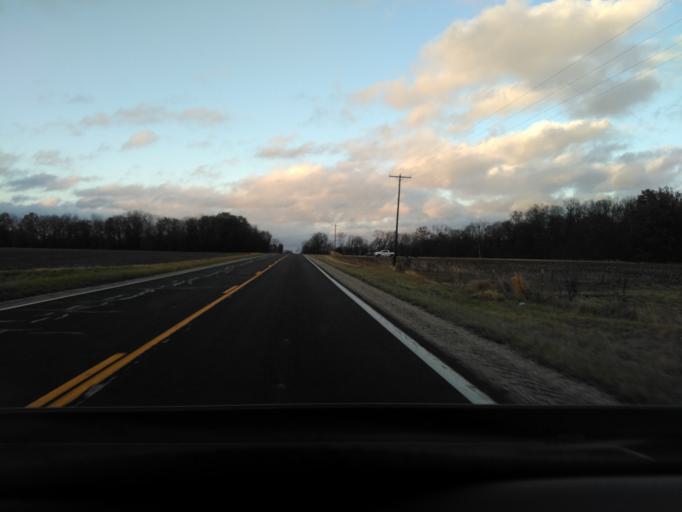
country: US
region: Illinois
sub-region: Effingham County
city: Altamont
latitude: 38.9776
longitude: -88.7489
